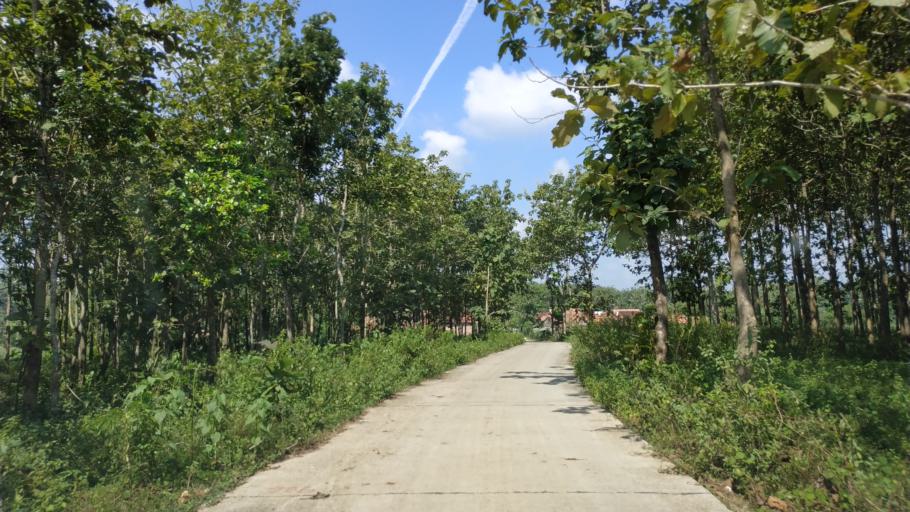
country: ID
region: Central Java
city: Guyangan
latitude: -7.0032
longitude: 111.0902
